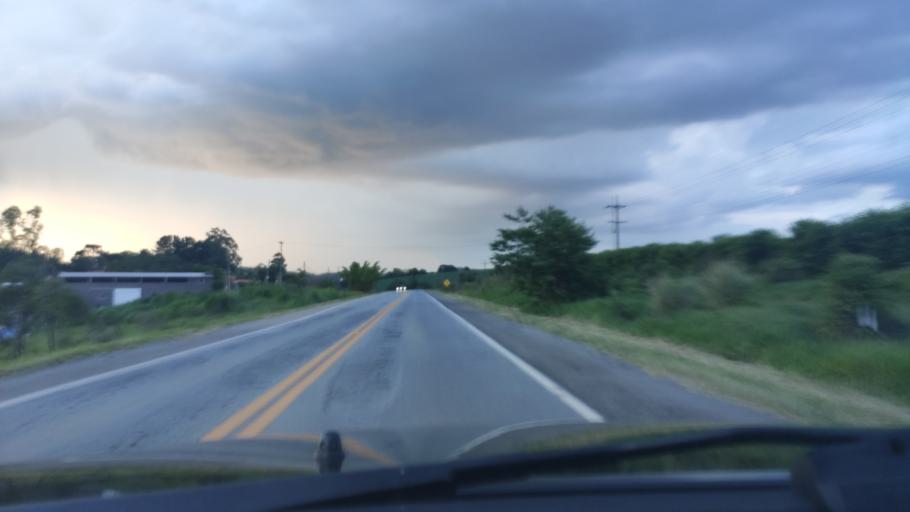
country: BR
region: Sao Paulo
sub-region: Braganca Paulista
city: Braganca Paulista
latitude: -22.8632
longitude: -46.5376
